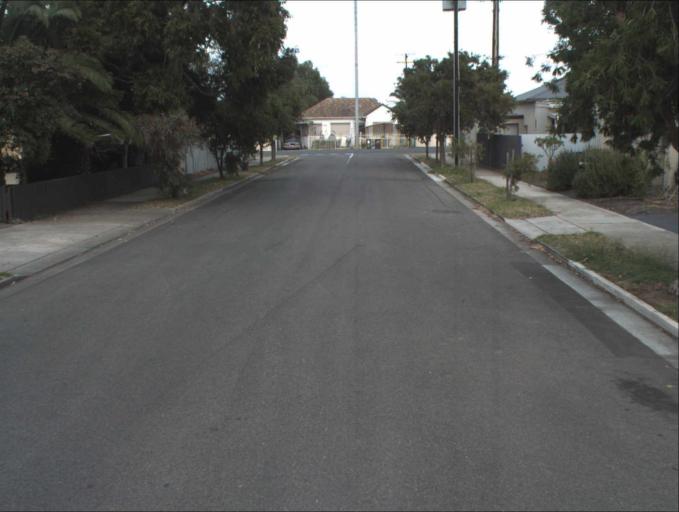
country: AU
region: South Australia
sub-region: Port Adelaide Enfield
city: Birkenhead
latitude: -34.8276
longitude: 138.4965
